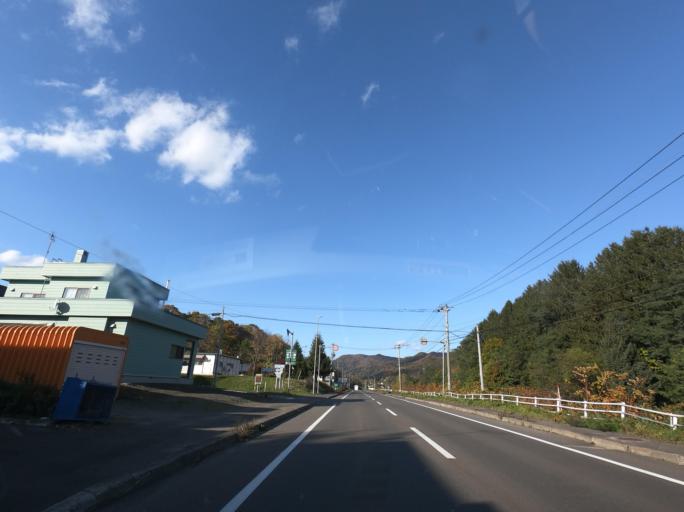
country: JP
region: Hokkaido
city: Iwamizawa
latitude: 42.9865
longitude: 142.0067
